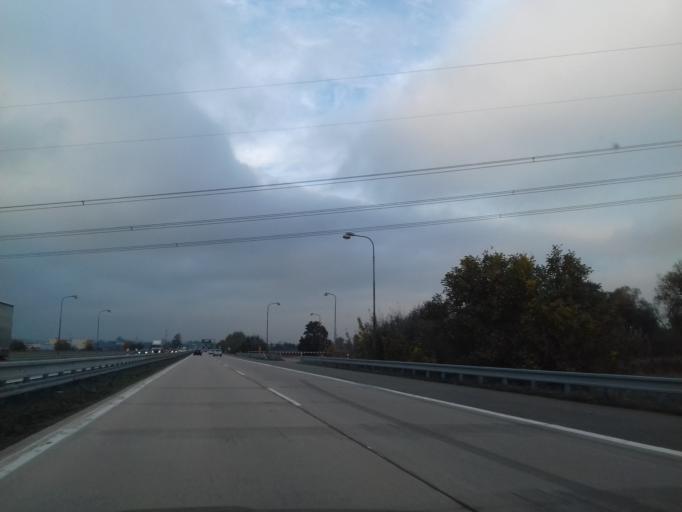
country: CZ
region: South Moravian
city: Rajhradice
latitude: 49.1220
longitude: 16.6451
